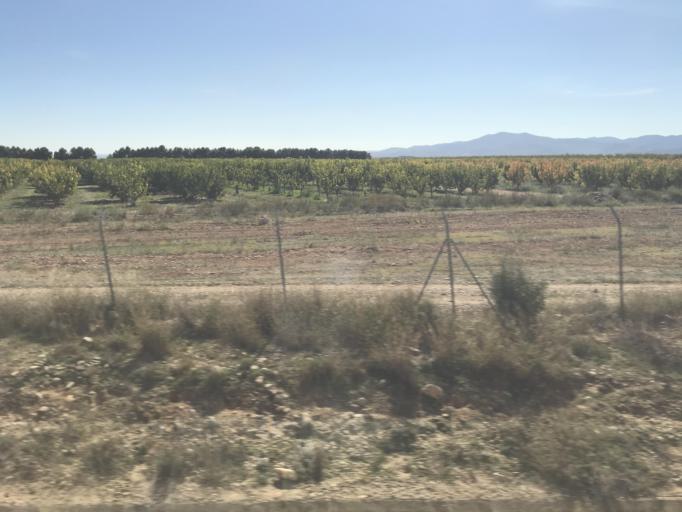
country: ES
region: Aragon
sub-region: Provincia de Zaragoza
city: Calatorao
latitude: 41.5338
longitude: -1.3767
